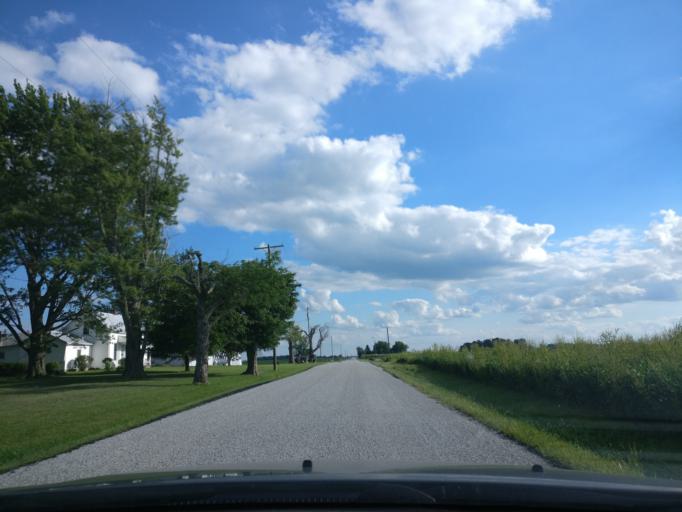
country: US
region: Ohio
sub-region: Clinton County
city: Wilmington
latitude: 39.5141
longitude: -83.7836
